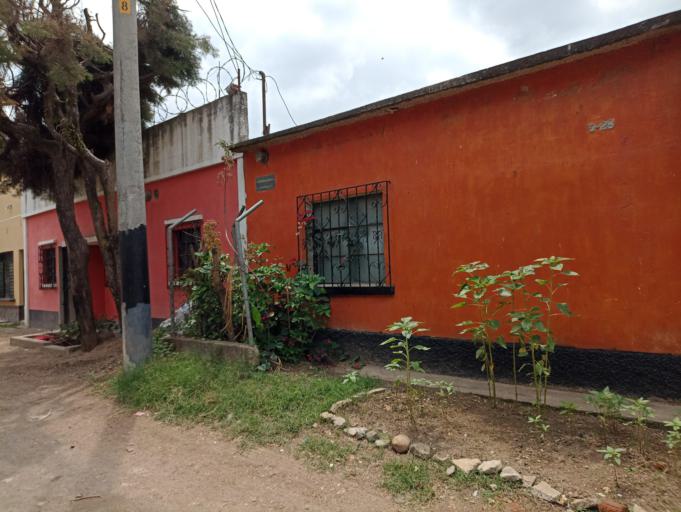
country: GT
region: Guatemala
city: Villa Canales
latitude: 14.4884
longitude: -90.5375
